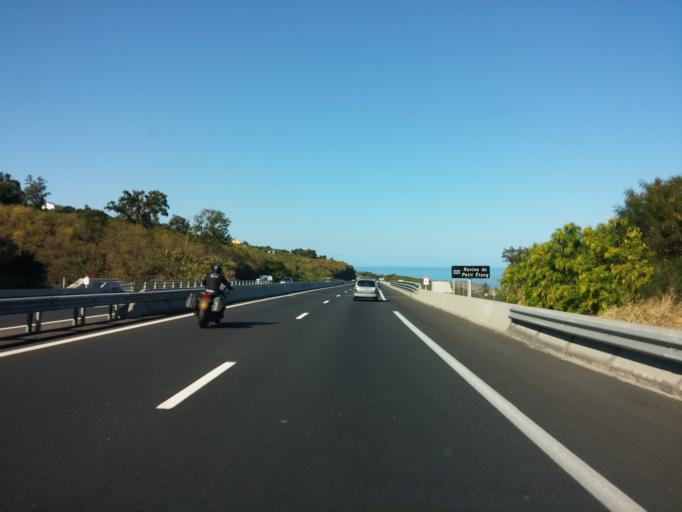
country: RE
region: Reunion
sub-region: Reunion
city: Saint-Leu
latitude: -21.1689
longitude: 55.2984
